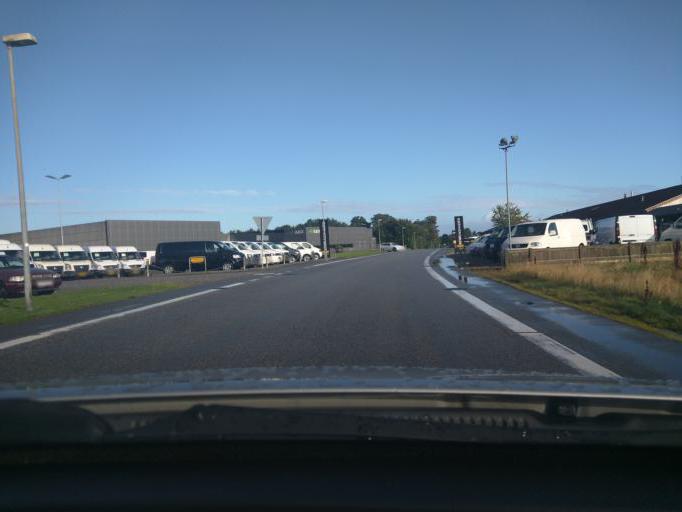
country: DK
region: Central Jutland
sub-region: Viborg Kommune
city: Viborg
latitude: 56.4672
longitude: 9.3983
